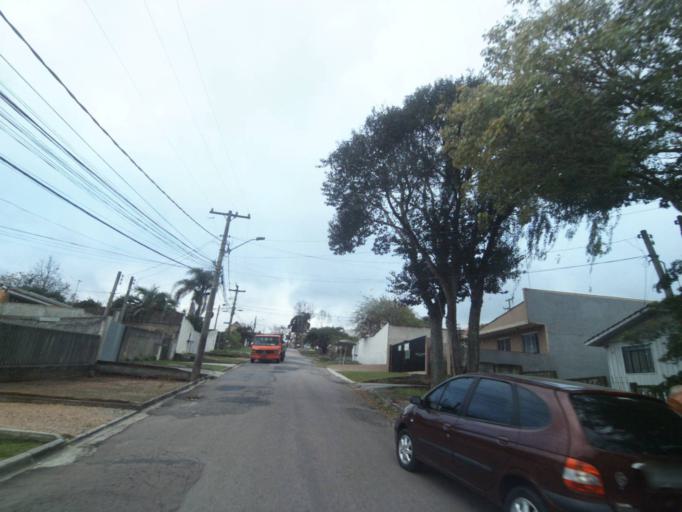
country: BR
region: Parana
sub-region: Curitiba
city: Curitiba
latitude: -25.5199
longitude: -49.3091
